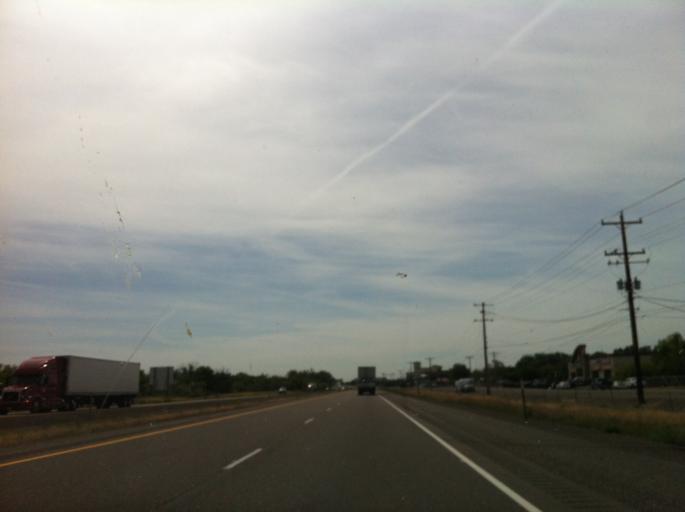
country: US
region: Oregon
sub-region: Malheur County
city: Ontario
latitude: 44.0460
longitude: -116.9733
